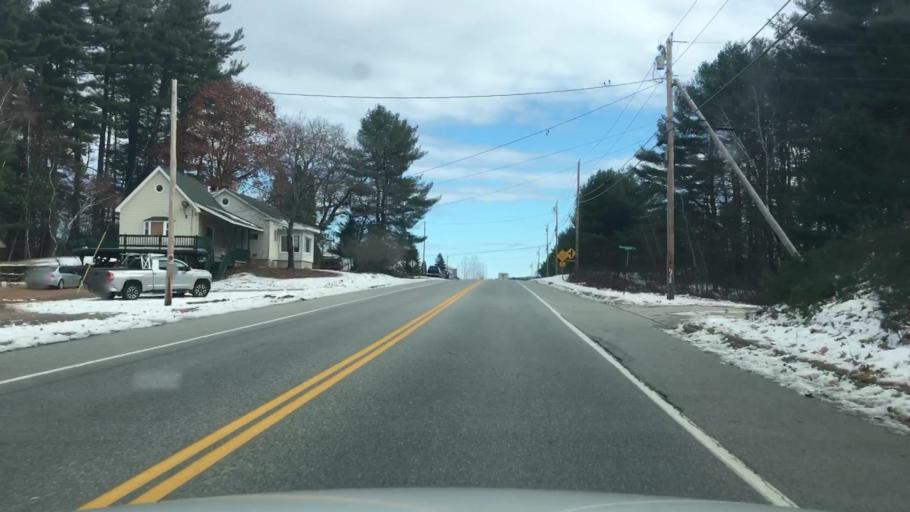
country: US
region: Maine
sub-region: Androscoggin County
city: Livermore
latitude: 44.3873
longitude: -70.2442
